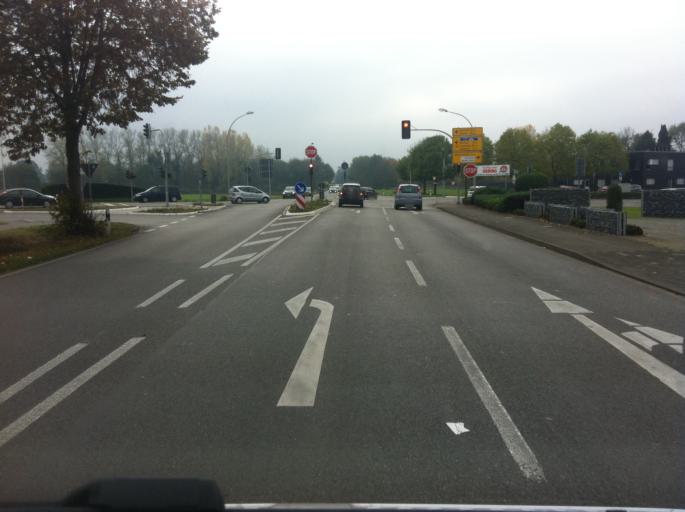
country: DE
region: North Rhine-Westphalia
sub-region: Regierungsbezirk Munster
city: Sudlohn
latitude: 51.9345
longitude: 6.8184
